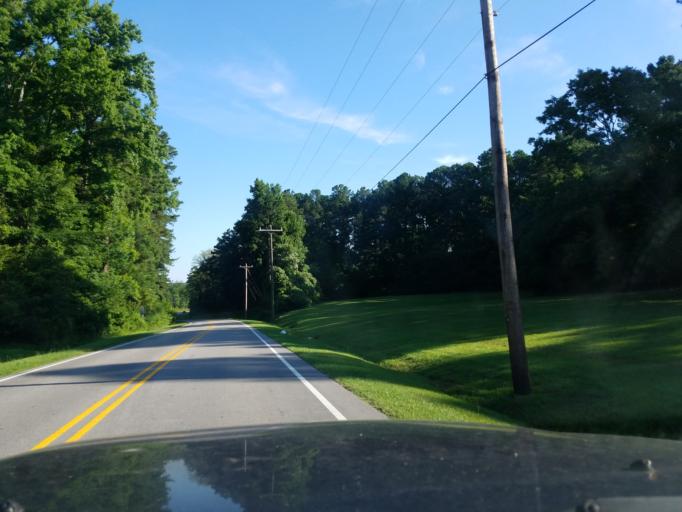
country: US
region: North Carolina
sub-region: Granville County
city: Butner
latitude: 36.1433
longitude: -78.7671
